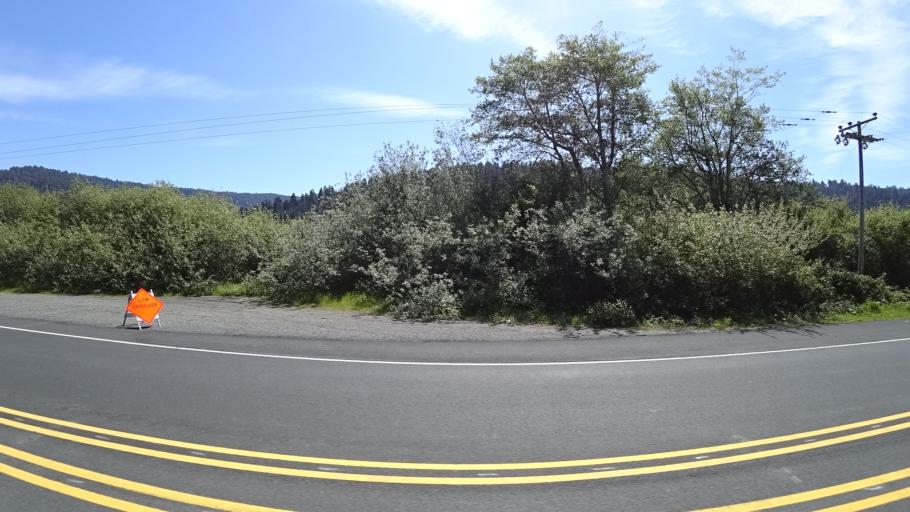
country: US
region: California
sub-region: Humboldt County
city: Westhaven-Moonstone
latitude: 41.2961
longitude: -124.0544
